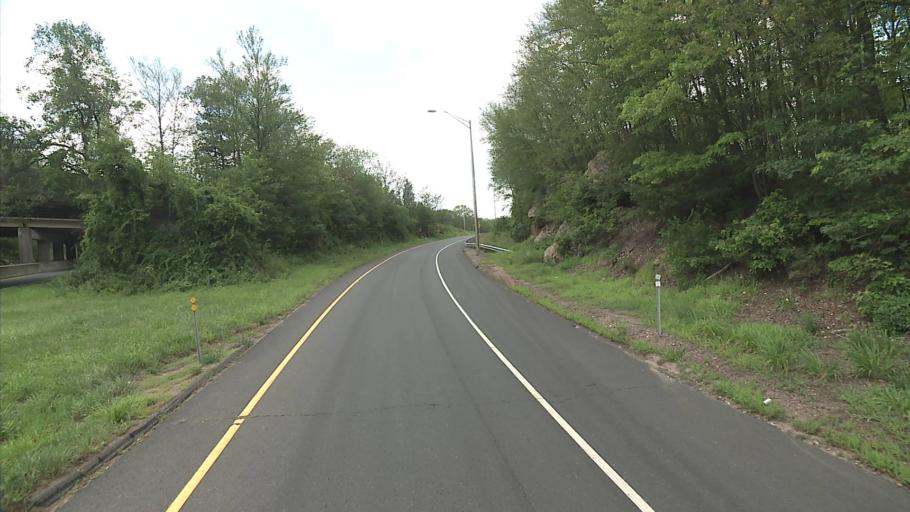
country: US
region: Connecticut
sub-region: Middlesex County
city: Higganum
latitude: 41.5127
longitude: -72.5972
